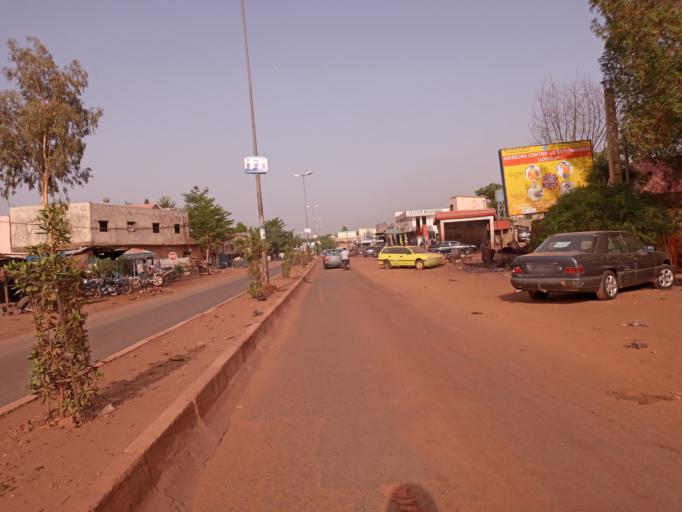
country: ML
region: Bamako
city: Bamako
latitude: 12.6614
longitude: -7.9787
